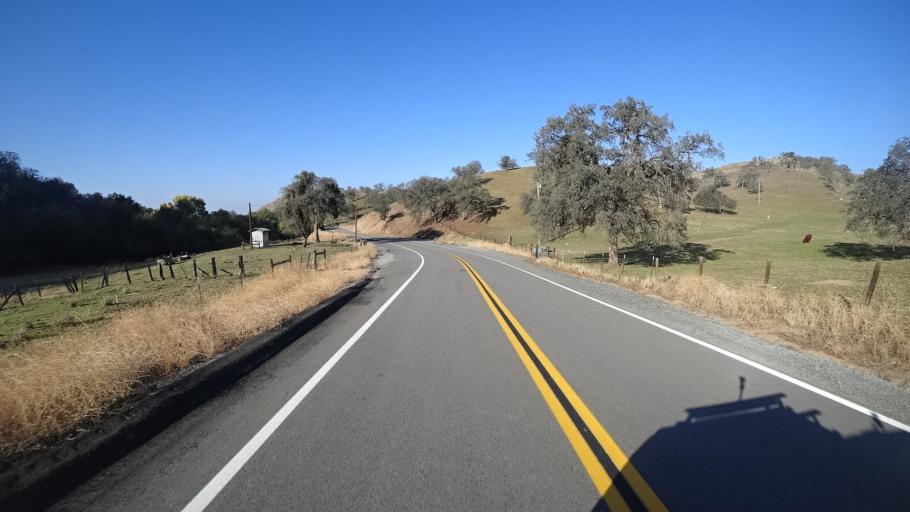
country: US
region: California
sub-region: Kern County
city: Alta Sierra
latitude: 35.7145
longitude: -118.8184
